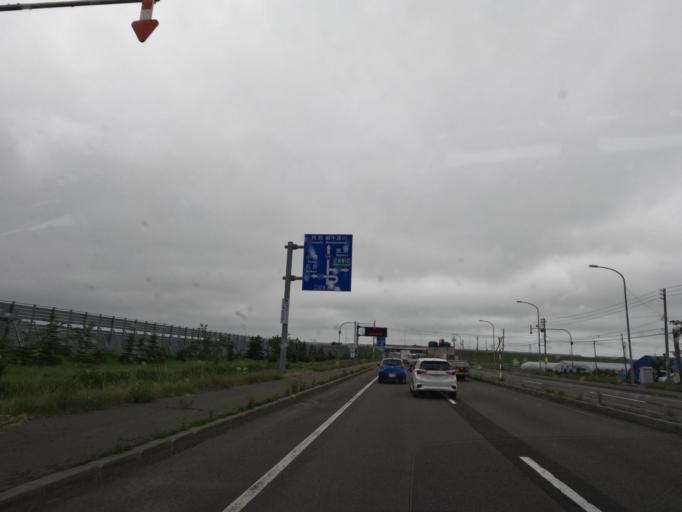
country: JP
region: Hokkaido
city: Tobetsu
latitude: 43.1809
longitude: 141.5229
